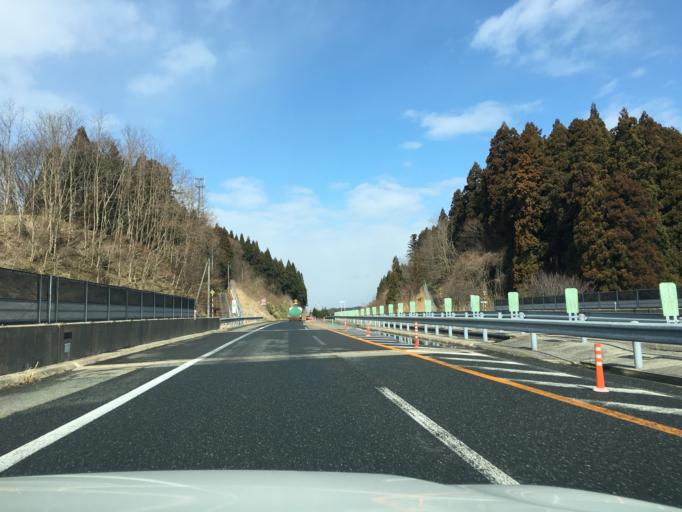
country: JP
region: Akita
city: Akita Shi
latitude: 39.7876
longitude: 140.1060
